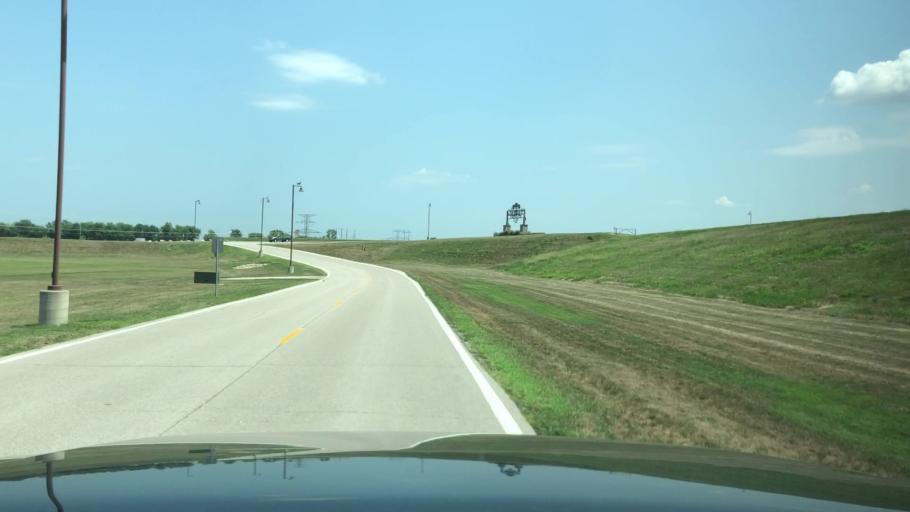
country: US
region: Missouri
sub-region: Saint Charles County
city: Saint Peters
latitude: 38.8214
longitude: -90.5658
